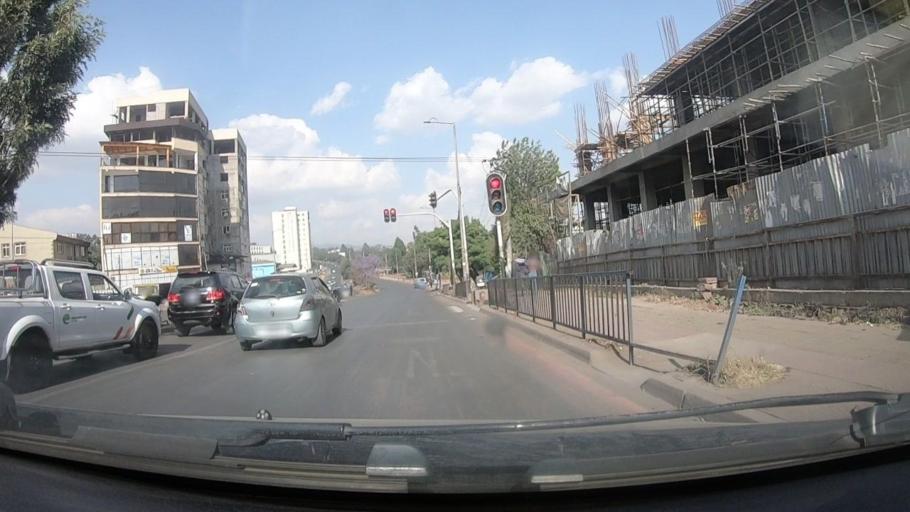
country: ET
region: Adis Abeba
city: Addis Ababa
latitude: 8.9734
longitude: 38.7317
